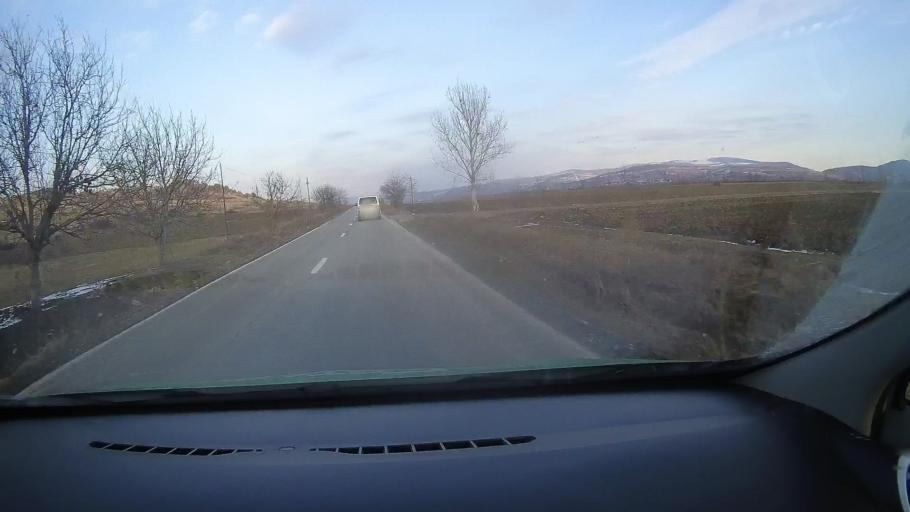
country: RO
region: Mures
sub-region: Comuna Vanatori
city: Vanatori
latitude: 46.2532
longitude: 24.9425
